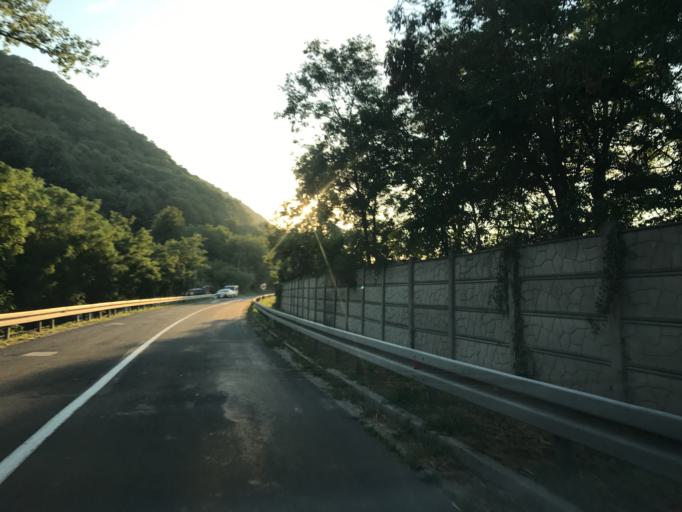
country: RO
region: Caras-Severin
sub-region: Comuna Berzasca
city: Berzasca
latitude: 44.6294
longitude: 21.9594
